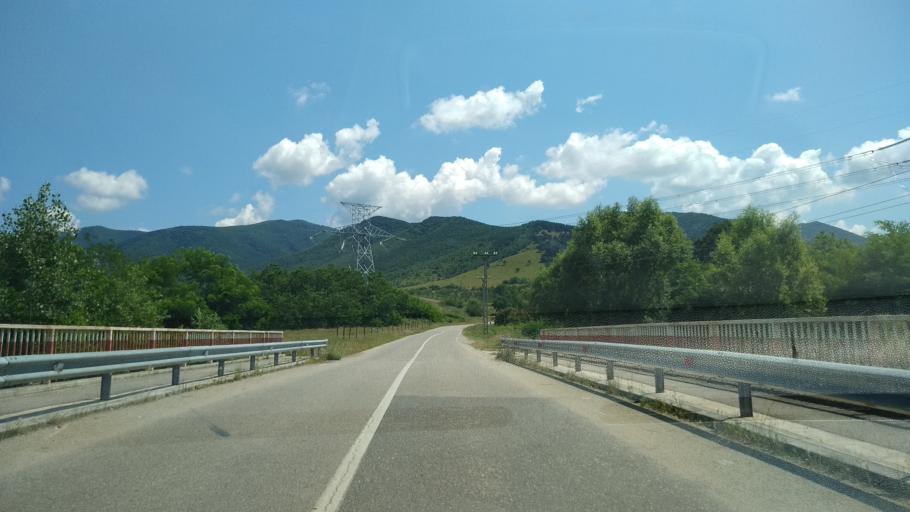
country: RO
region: Hunedoara
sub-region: Comuna Santamaria-Orlea
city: Santamaria-Orlea
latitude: 45.5891
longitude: 22.9900
